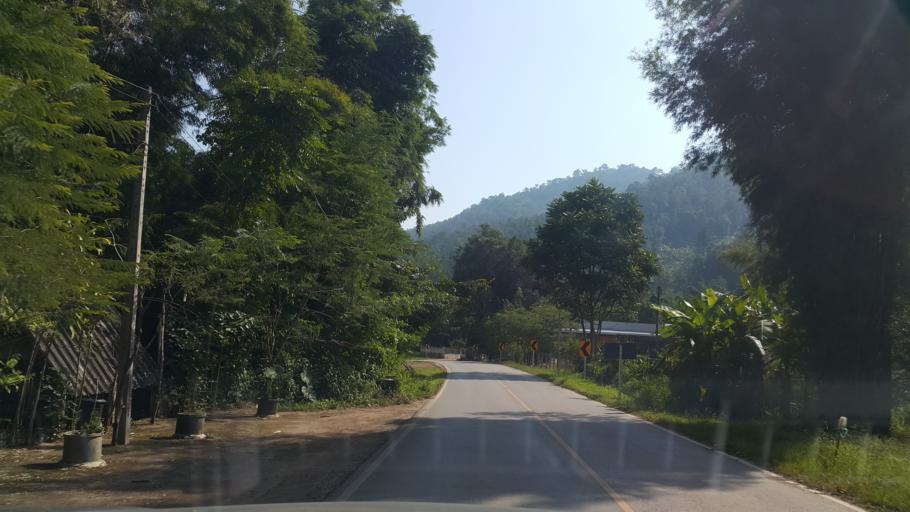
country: TH
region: Chiang Mai
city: Samoeng
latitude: 18.8675
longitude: 98.7208
